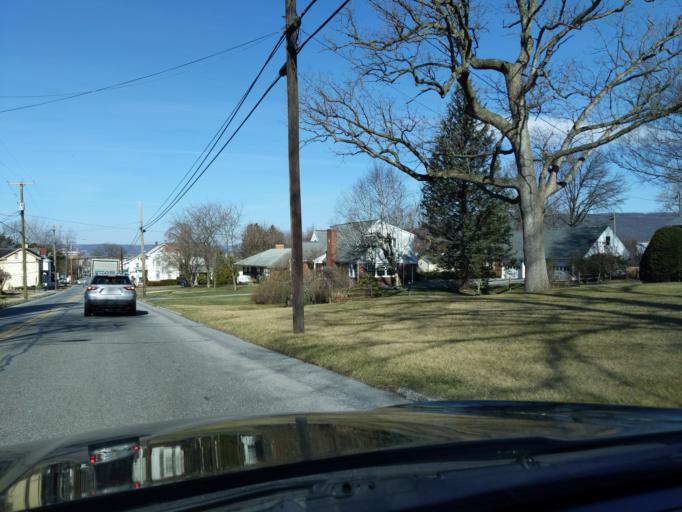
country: US
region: Pennsylvania
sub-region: Blair County
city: Martinsburg
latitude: 40.3096
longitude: -78.3195
